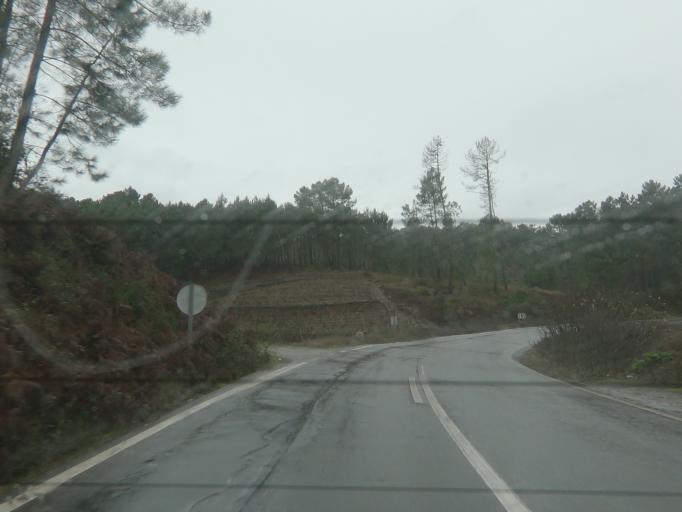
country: PT
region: Vila Real
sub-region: Vila Real
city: Vila Real
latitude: 41.2586
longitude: -7.6887
